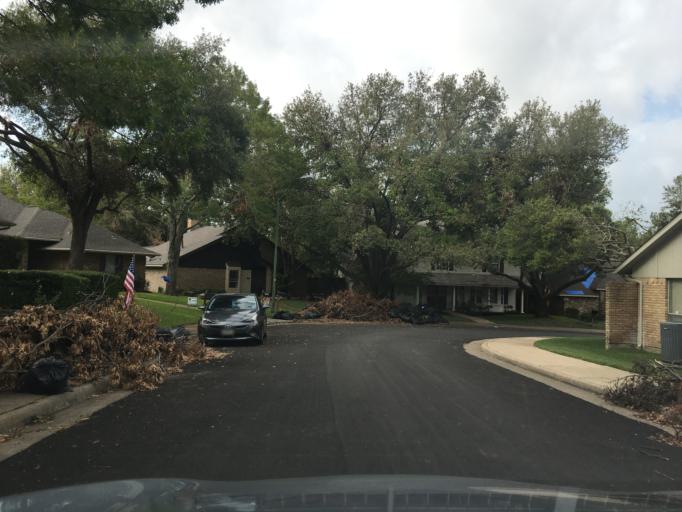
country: US
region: Texas
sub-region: Dallas County
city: Richardson
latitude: 32.8968
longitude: -96.7497
